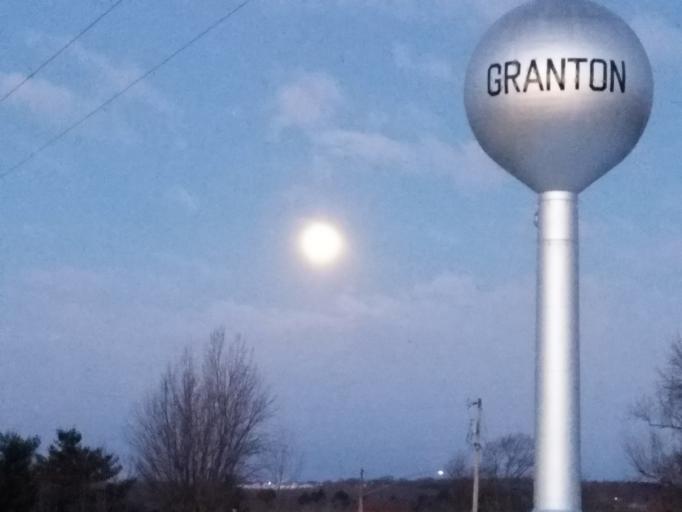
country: US
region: Wisconsin
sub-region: Clark County
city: Neillsville
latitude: 44.5820
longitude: -90.4578
